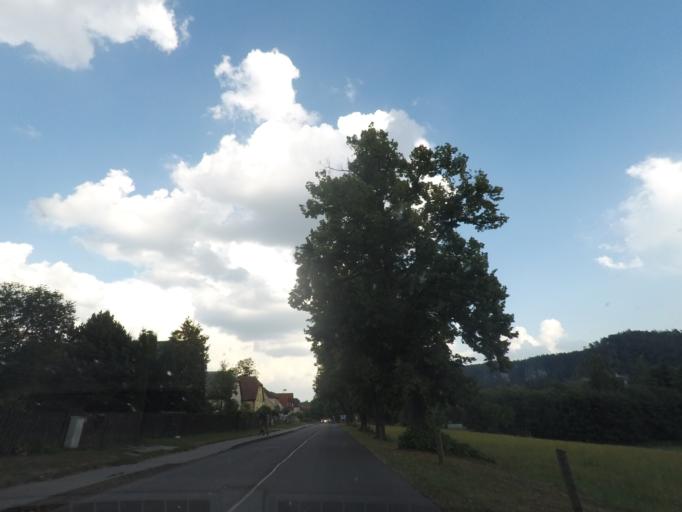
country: CZ
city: Teplice nad Metuji
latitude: 50.6185
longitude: 16.1179
